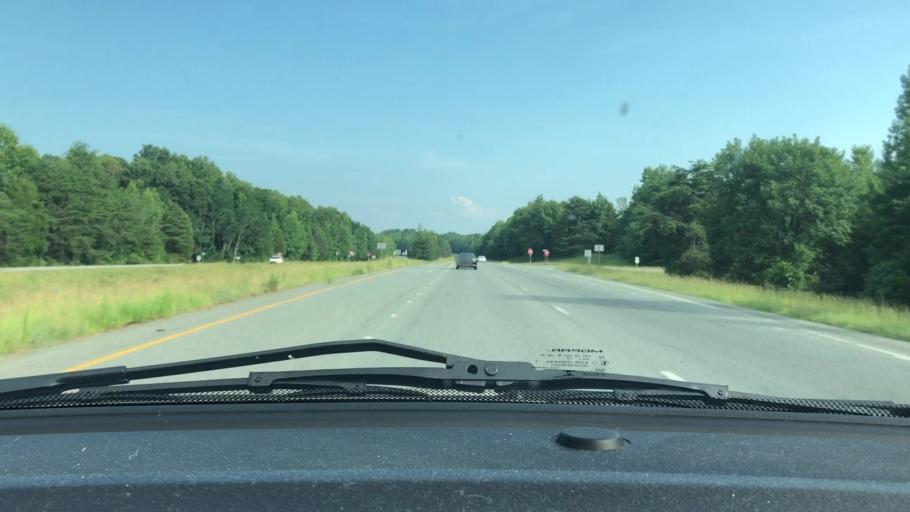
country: US
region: North Carolina
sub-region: Randolph County
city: Liberty
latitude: 35.8758
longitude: -79.6329
